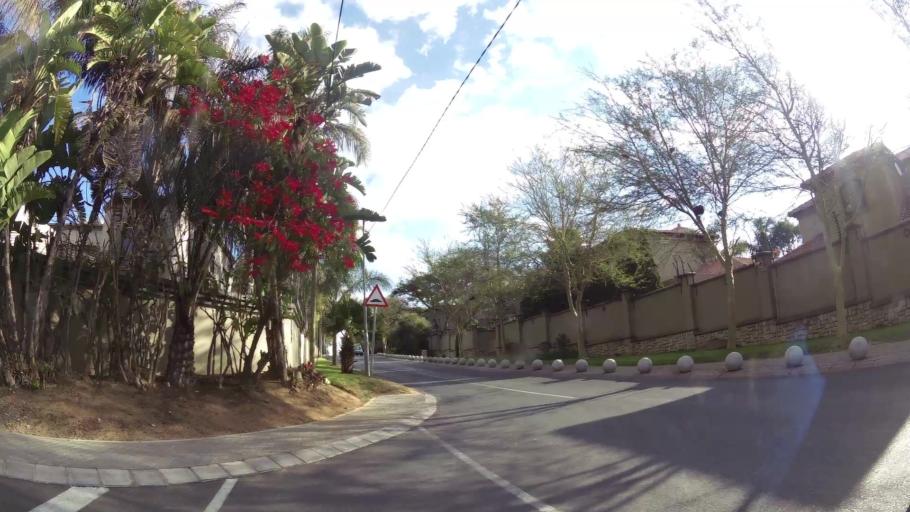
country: ZA
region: Gauteng
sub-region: City of Johannesburg Metropolitan Municipality
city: Diepsloot
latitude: -26.0002
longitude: 28.0173
